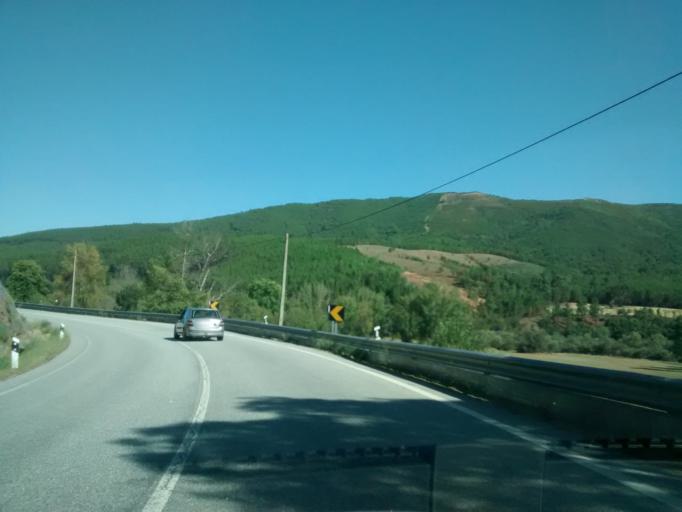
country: PT
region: Castelo Branco
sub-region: Covilha
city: Teixoso
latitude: 40.3939
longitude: -7.4293
